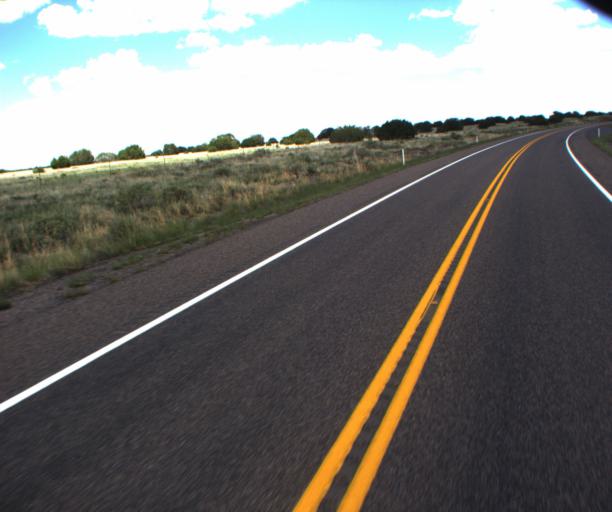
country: US
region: Arizona
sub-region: Apache County
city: Springerville
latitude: 34.1451
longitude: -109.2213
